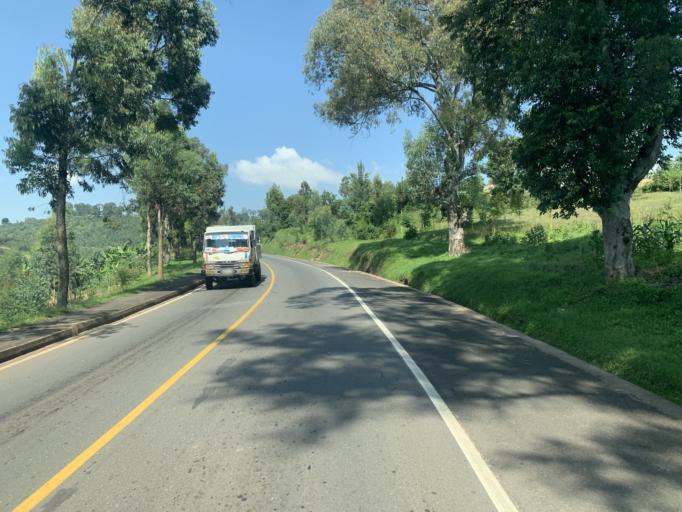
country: RW
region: Kigali
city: Kigali
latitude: -1.9933
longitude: 29.9237
